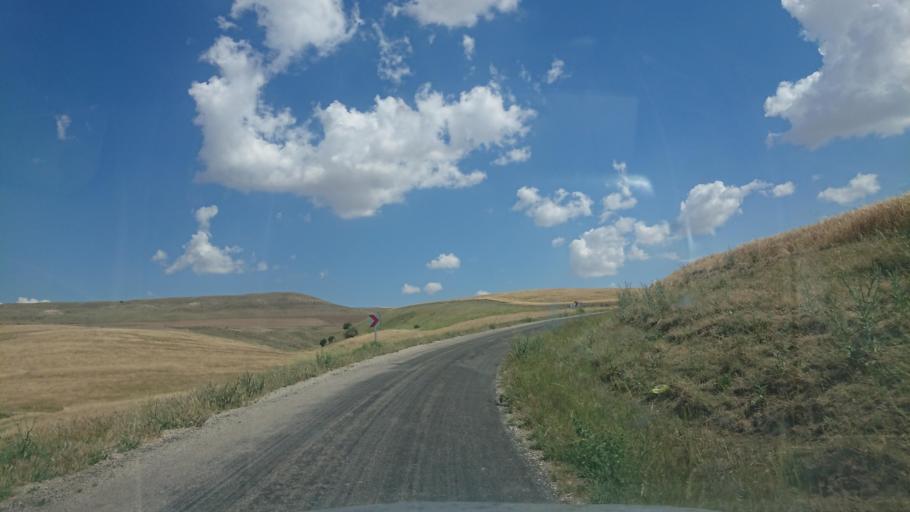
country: TR
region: Aksaray
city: Agacoren
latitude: 38.8130
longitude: 33.8002
